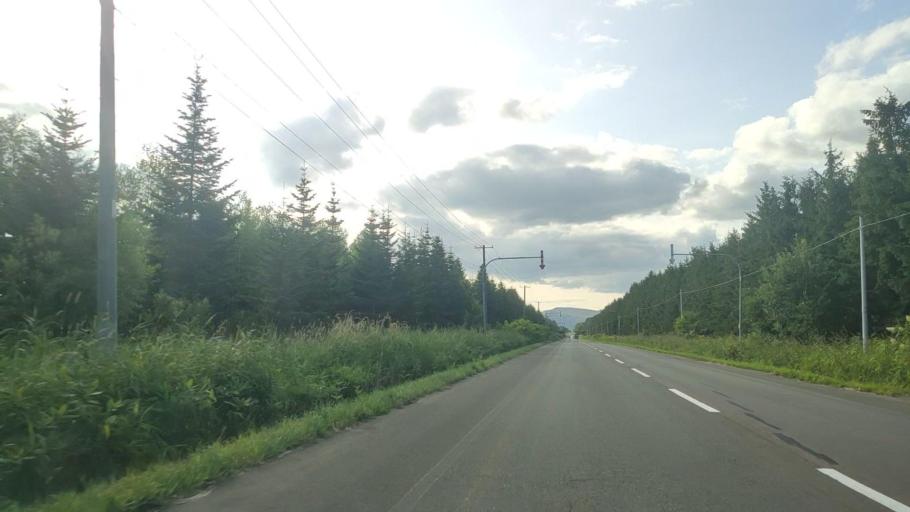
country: JP
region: Hokkaido
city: Makubetsu
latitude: 44.8867
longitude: 142.0086
